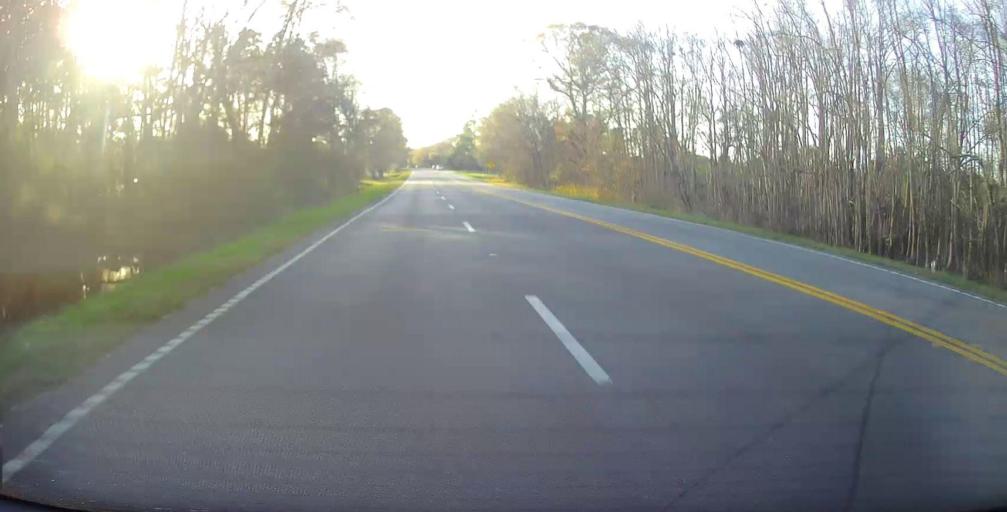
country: US
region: Georgia
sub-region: Evans County
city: Claxton
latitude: 32.1518
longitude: -81.8020
